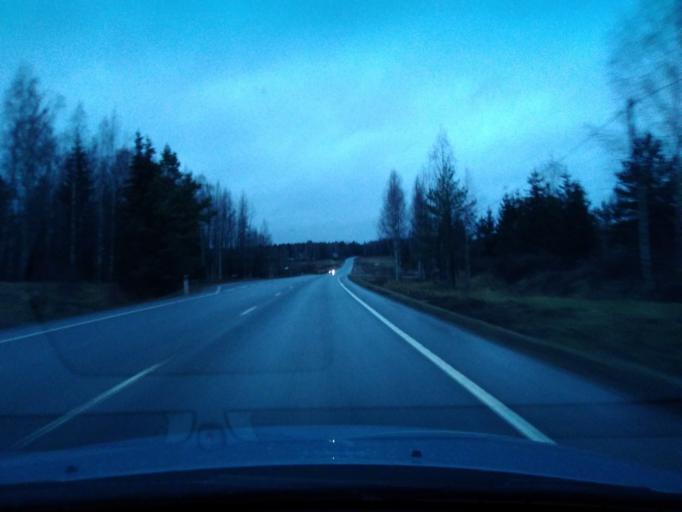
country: FI
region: Uusimaa
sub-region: Porvoo
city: Porvoo
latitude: 60.4110
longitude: 25.5825
